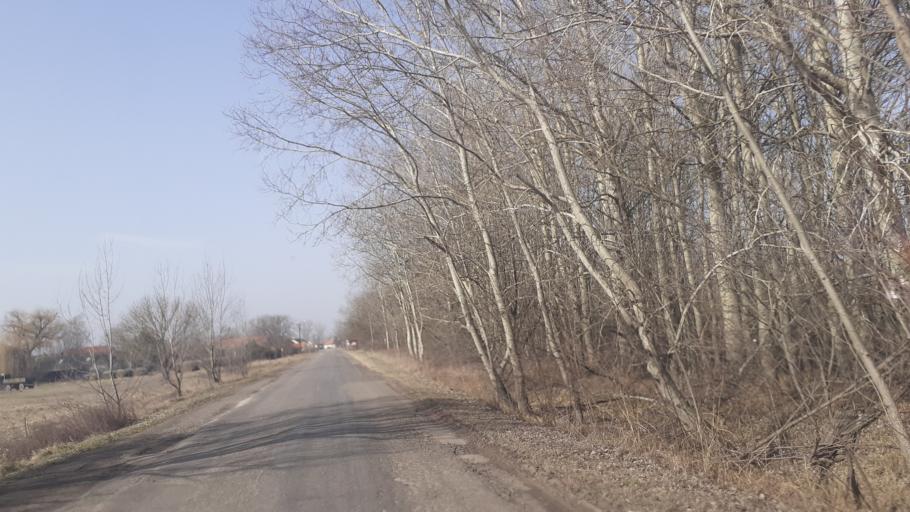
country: HU
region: Pest
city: Dabas
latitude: 47.0626
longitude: 19.2854
